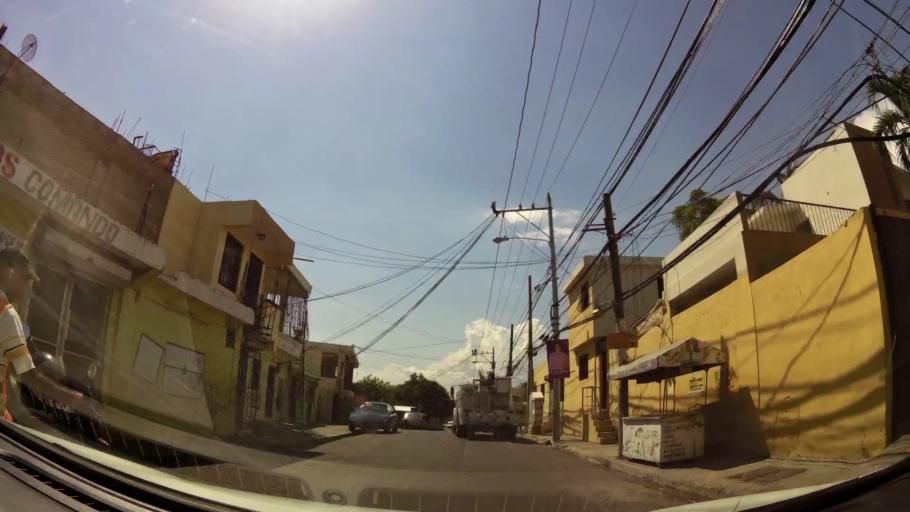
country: DO
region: Nacional
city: Bella Vista
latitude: 18.4645
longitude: -69.9768
